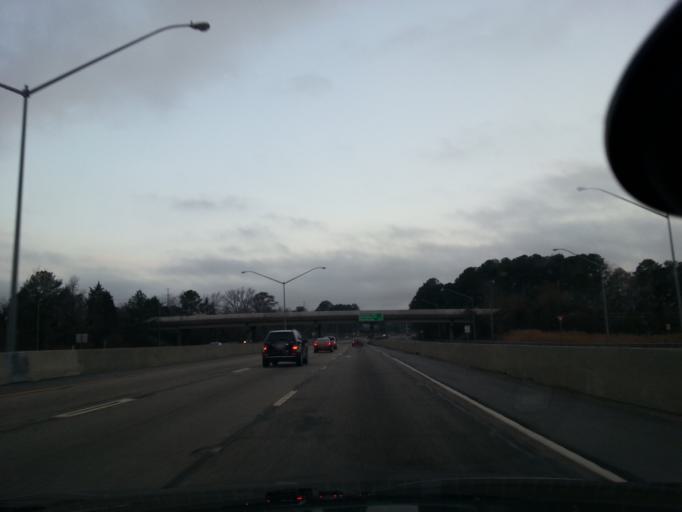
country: US
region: Virginia
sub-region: City of Chesapeake
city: Chesapeake
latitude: 36.8431
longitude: -76.2119
